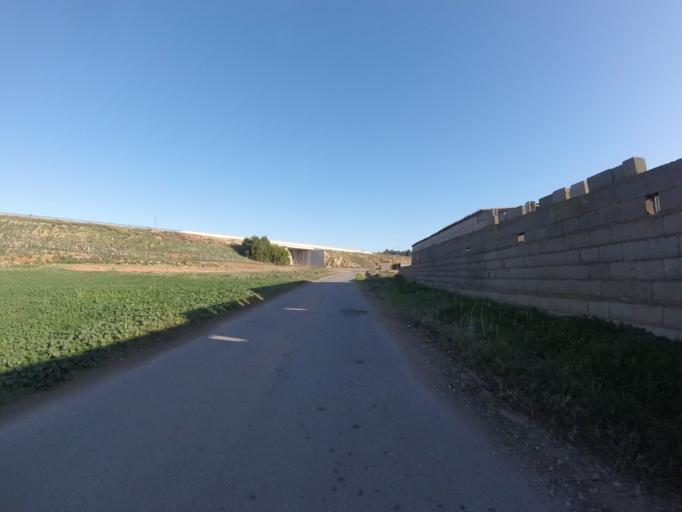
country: ES
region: Valencia
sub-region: Provincia de Castello
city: Torreblanca
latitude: 40.2305
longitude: 0.2018
